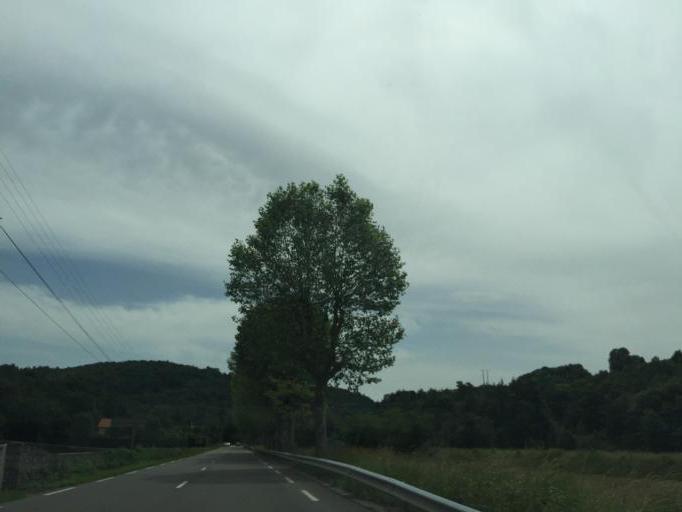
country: FR
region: Rhone-Alpes
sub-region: Departement de l'Ardeche
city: Saint-Marcel-les-Annonay
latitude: 45.2929
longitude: 4.6191
